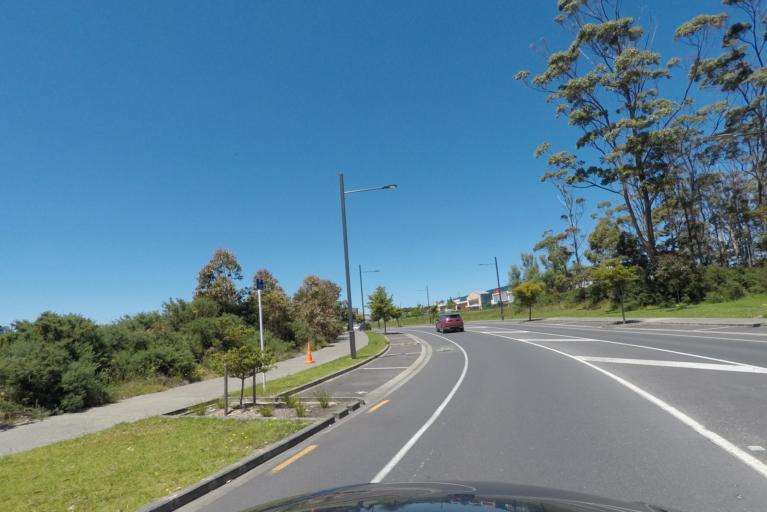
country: NZ
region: Auckland
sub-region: Auckland
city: Rosebank
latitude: -36.8176
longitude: 174.6082
